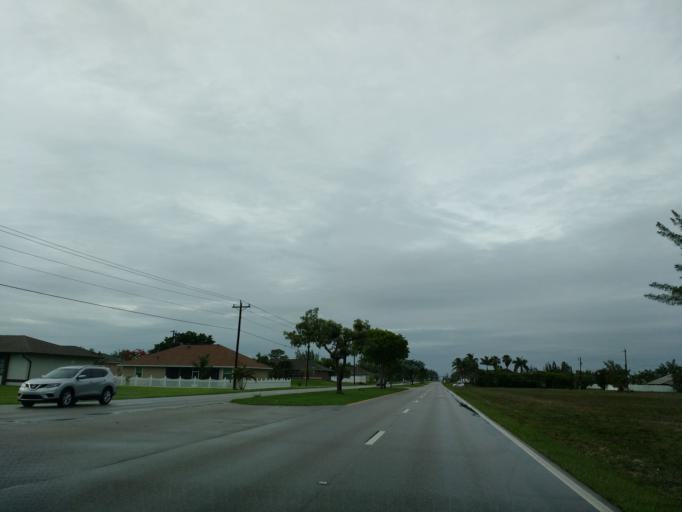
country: US
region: Florida
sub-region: Lee County
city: Cape Coral
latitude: 26.6172
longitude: -82.0071
